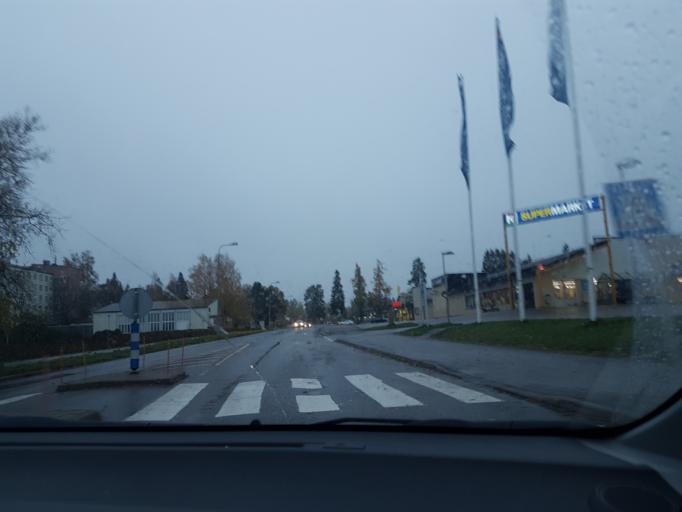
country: FI
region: Uusimaa
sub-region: Helsinki
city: Jaervenpaeae
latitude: 60.5306
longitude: 25.1087
